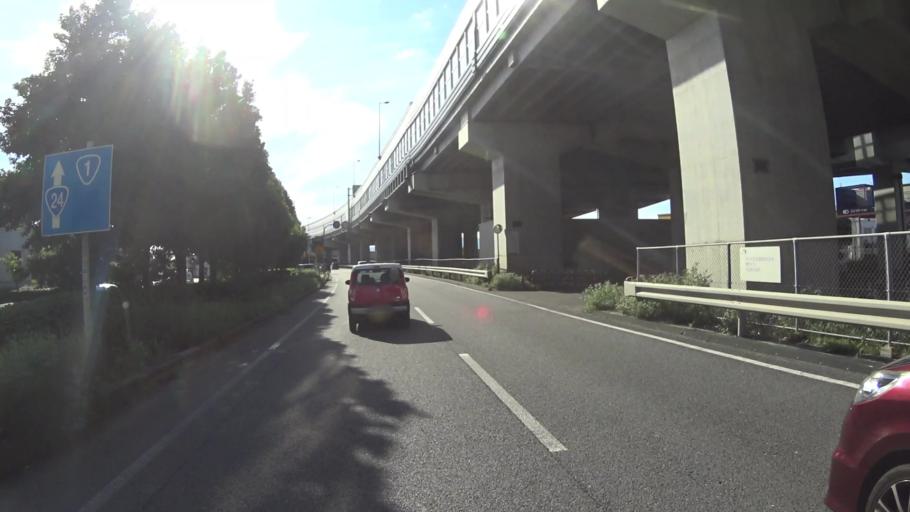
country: JP
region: Kyoto
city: Uji
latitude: 34.9051
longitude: 135.7794
